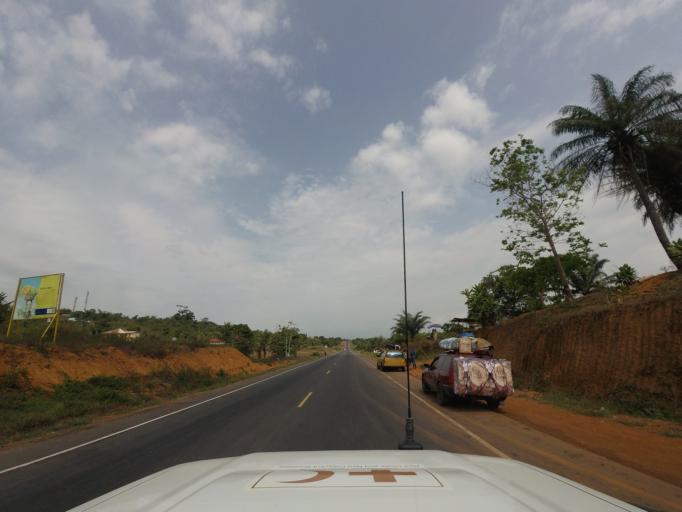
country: LR
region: Montserrado
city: Bensonville City
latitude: 6.4013
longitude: -10.5470
